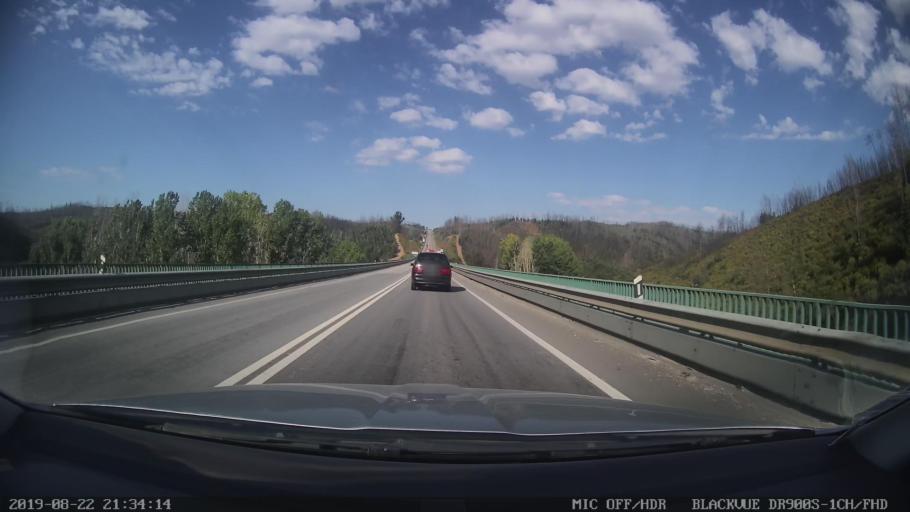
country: PT
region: Leiria
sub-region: Pedrogao Grande
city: Pedrogao Grande
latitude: 39.9275
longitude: -8.1887
